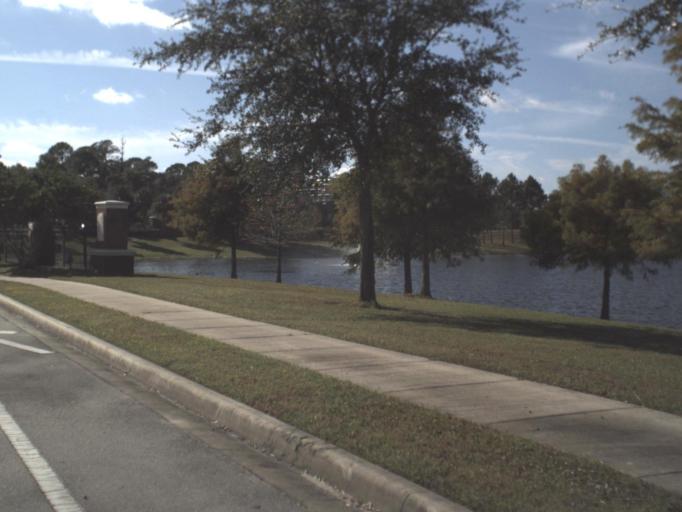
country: US
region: Florida
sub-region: Seminole County
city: Midway
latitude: 28.7595
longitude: -81.2407
